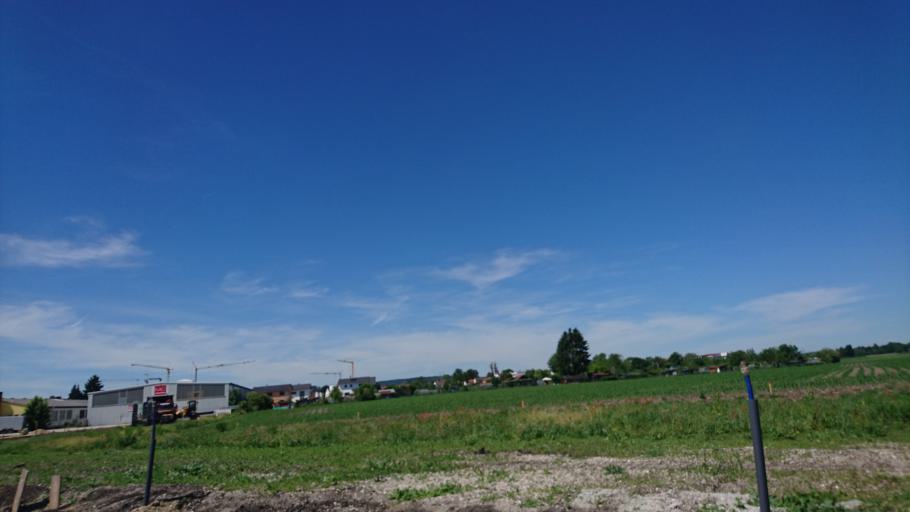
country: DE
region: Bavaria
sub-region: Lower Bavaria
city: Ergolding
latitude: 48.5703
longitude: 12.1799
